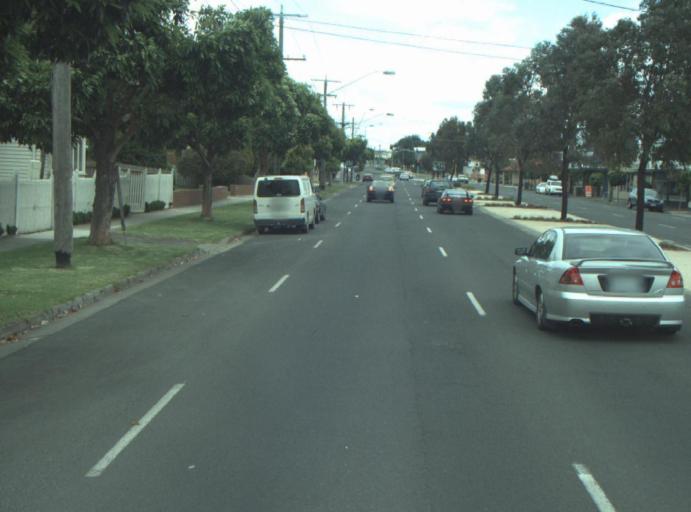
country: AU
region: Victoria
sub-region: Greater Geelong
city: East Geelong
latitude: -38.1566
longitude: 144.3730
